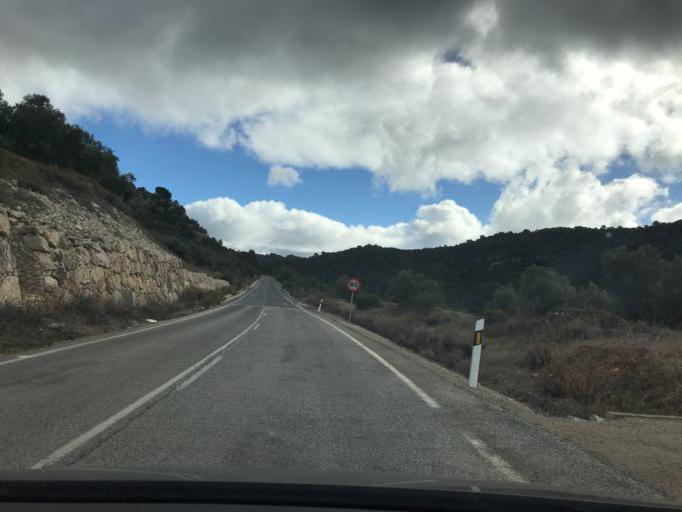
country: ES
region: Andalusia
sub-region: Provincia de Jaen
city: Cambil
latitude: 37.6912
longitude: -3.5066
